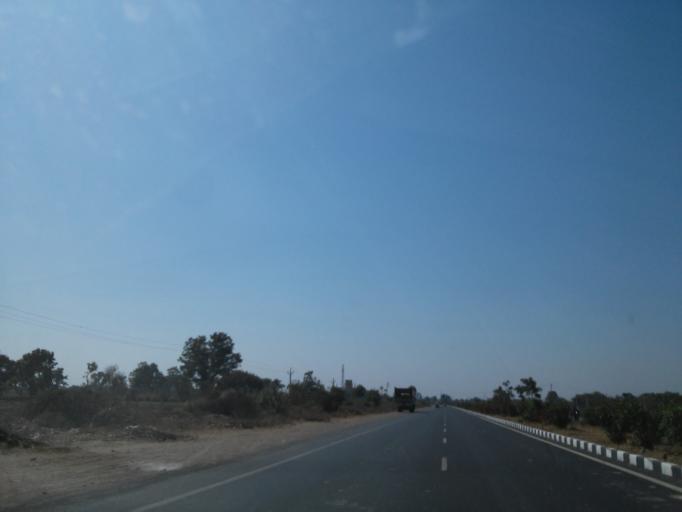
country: IN
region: Gujarat
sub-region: Sabar Kantha
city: Himatnagar
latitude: 23.5038
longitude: 72.9165
